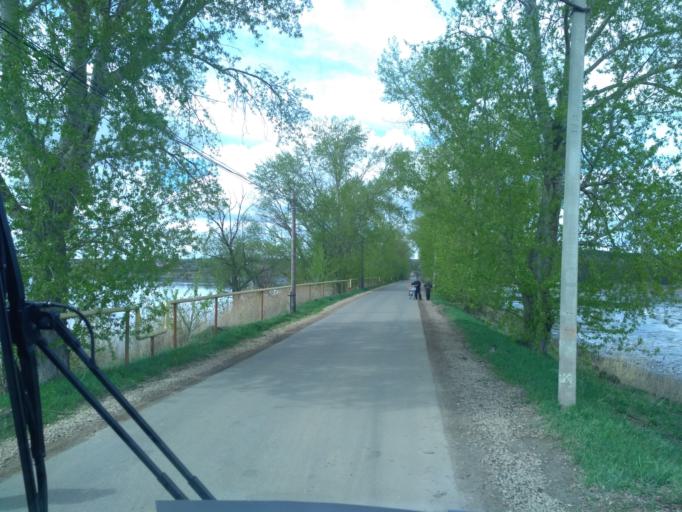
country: RU
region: Nizjnij Novgorod
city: Vad
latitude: 55.5375
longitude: 44.2031
